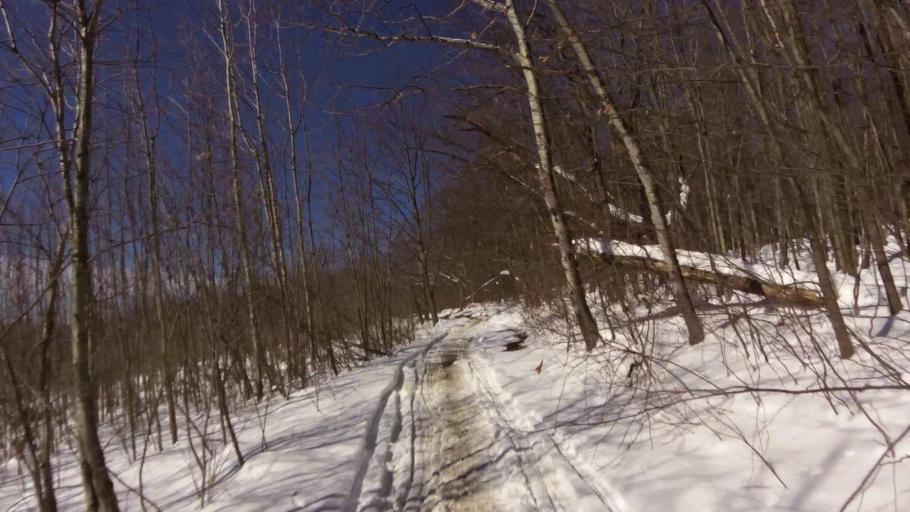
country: US
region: New York
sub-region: Allegany County
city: Cuba
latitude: 42.2792
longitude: -78.2369
